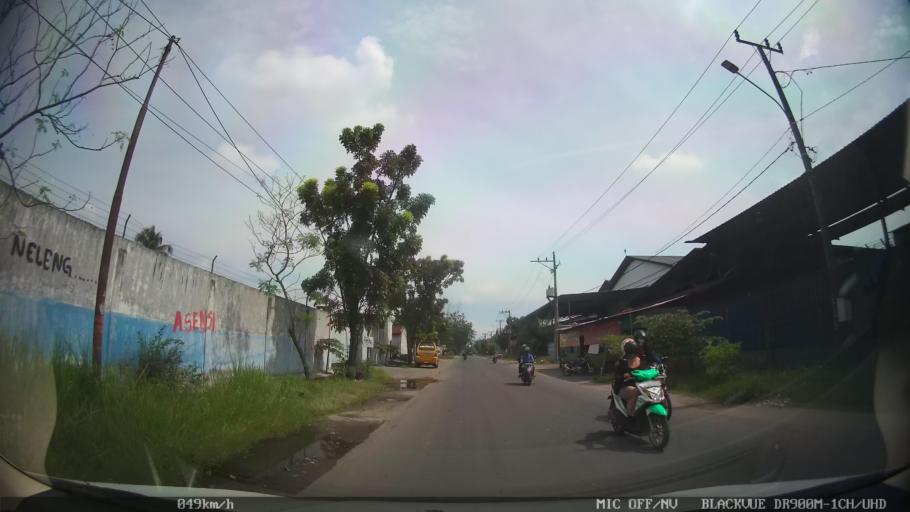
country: ID
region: North Sumatra
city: Medan
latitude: 3.6406
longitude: 98.7165
